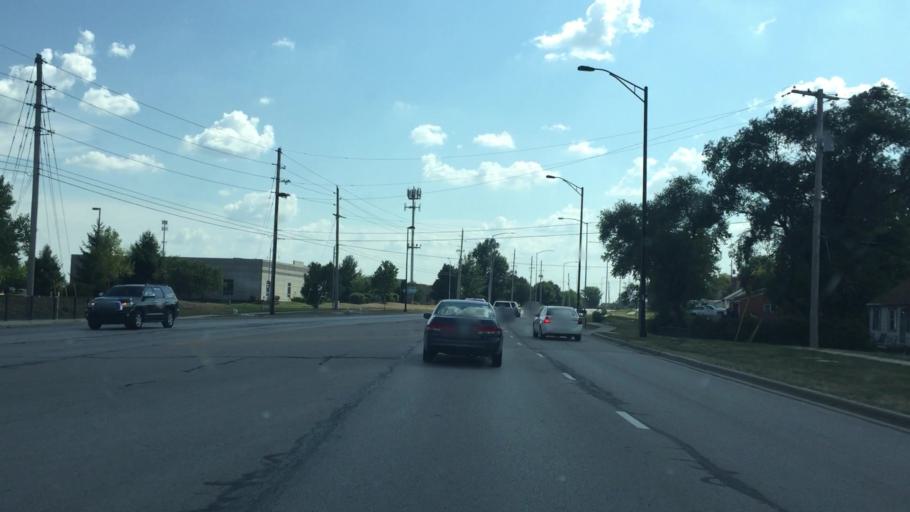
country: US
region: Kansas
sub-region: Johnson County
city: Olathe
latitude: 38.8960
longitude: -94.7920
